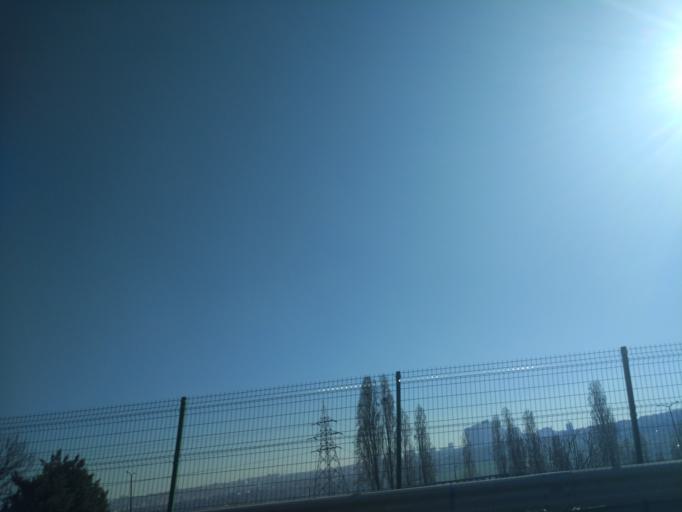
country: TR
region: Istanbul
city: Esenyurt
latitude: 41.0599
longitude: 28.7042
